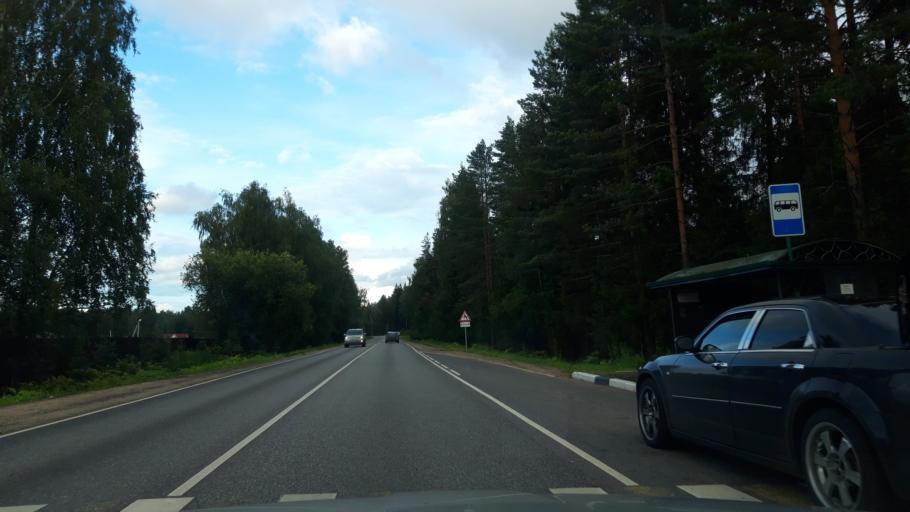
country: RU
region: Moskovskaya
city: Solnechnogorsk
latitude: 56.0959
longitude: 36.8593
